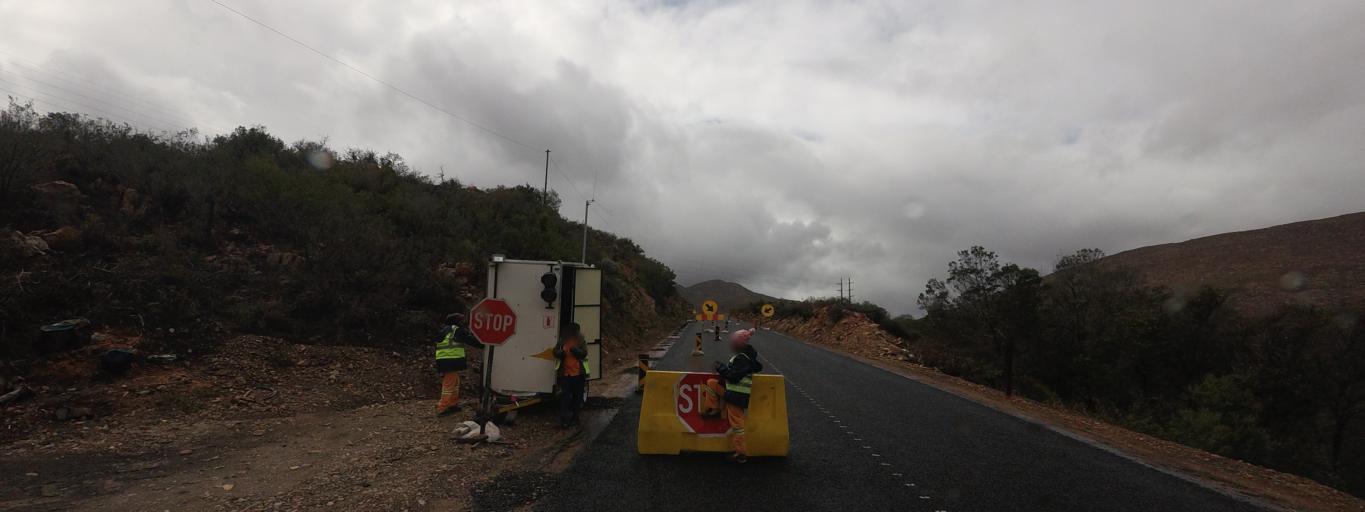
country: ZA
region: Western Cape
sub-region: Eden District Municipality
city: George
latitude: -33.8078
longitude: 22.3382
